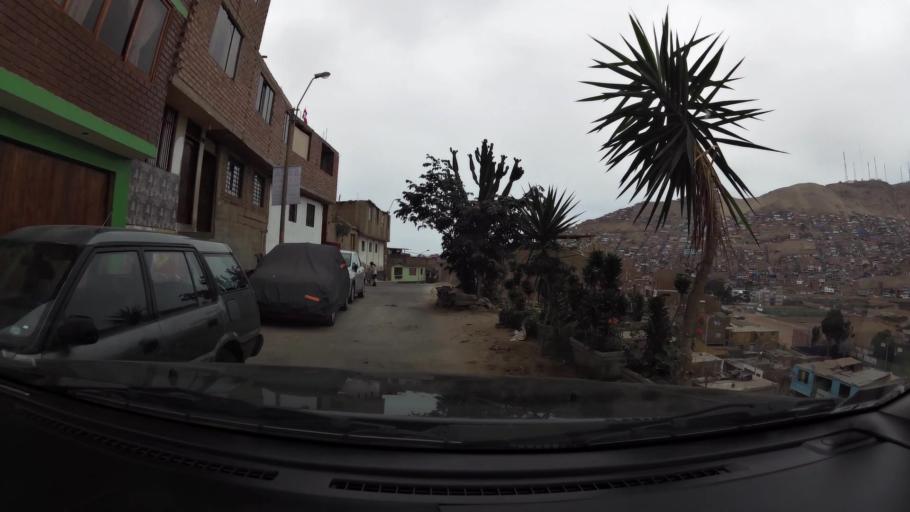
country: PE
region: Lima
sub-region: Lima
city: Surco
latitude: -12.1845
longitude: -77.0141
